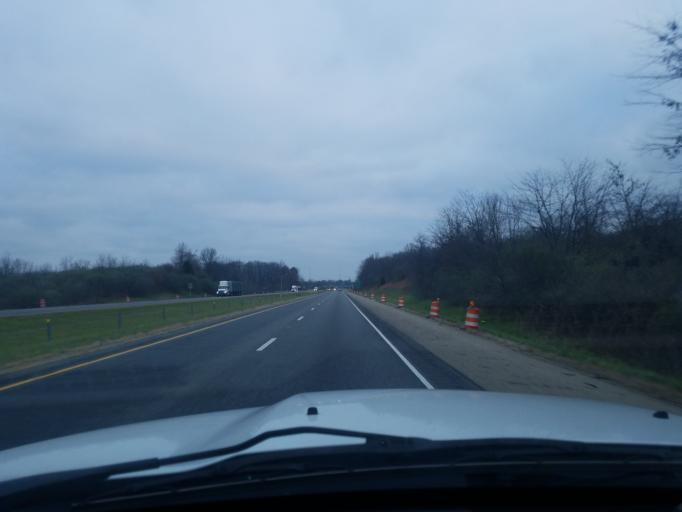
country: US
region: Indiana
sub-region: Delaware County
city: Yorktown
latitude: 40.2106
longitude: -85.5608
